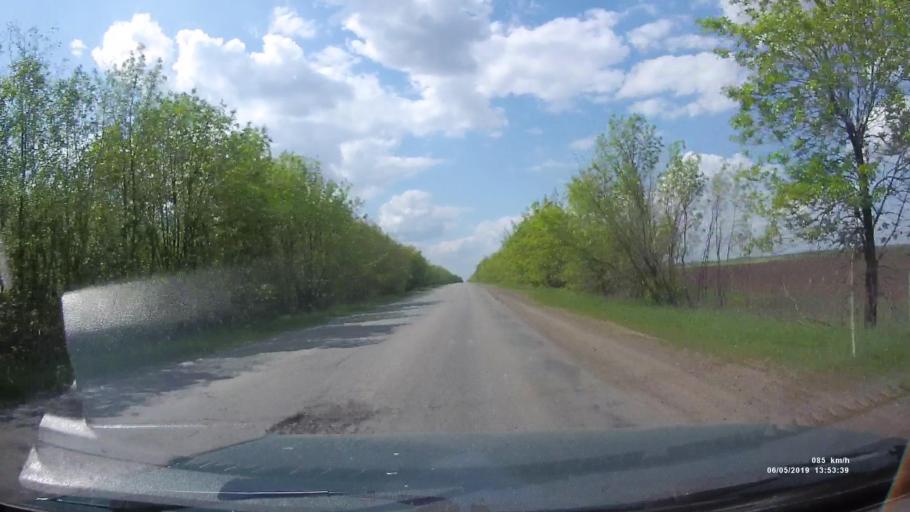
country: RU
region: Rostov
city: Melikhovskaya
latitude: 47.6695
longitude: 40.4593
